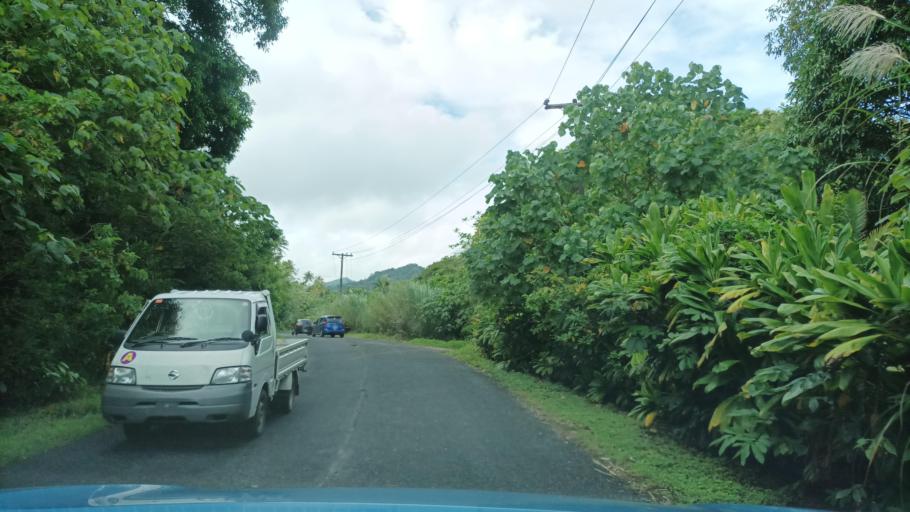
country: FM
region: Pohnpei
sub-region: Kolonia Municipality
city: Kolonia
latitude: 6.9676
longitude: 158.2514
